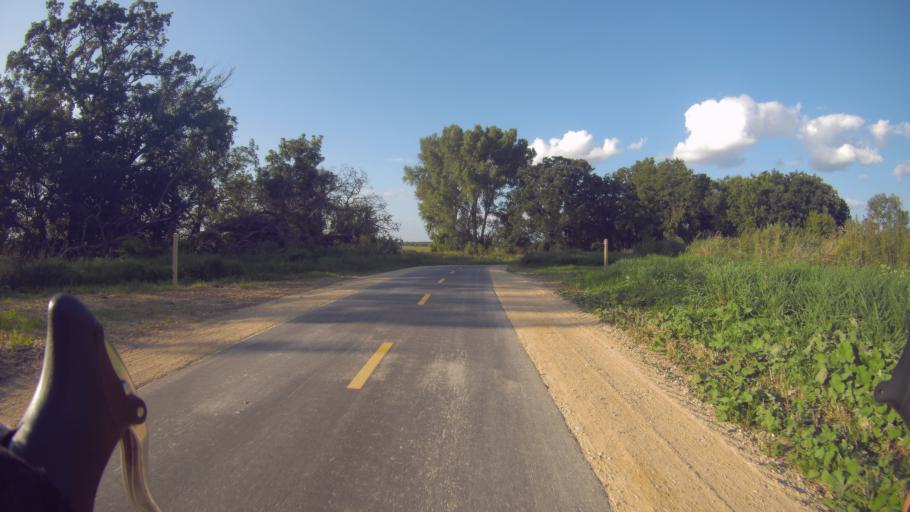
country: US
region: Wisconsin
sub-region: Dane County
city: Monona
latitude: 43.0264
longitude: -89.3376
